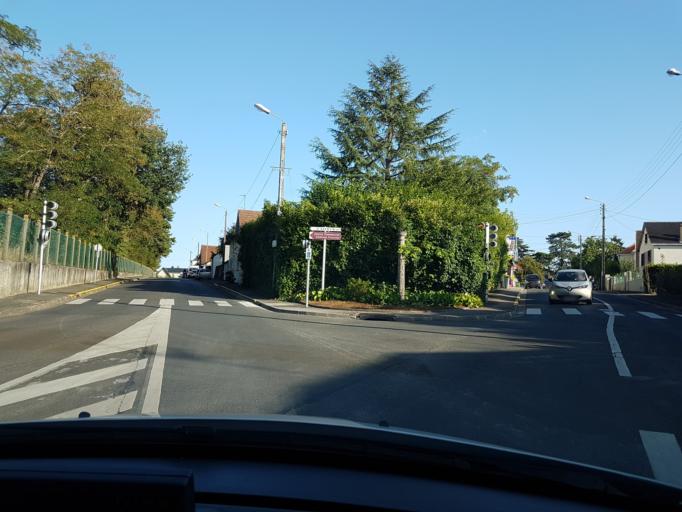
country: FR
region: Centre
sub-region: Departement d'Indre-et-Loire
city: Saint-Avertin
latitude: 47.3590
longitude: 0.7307
